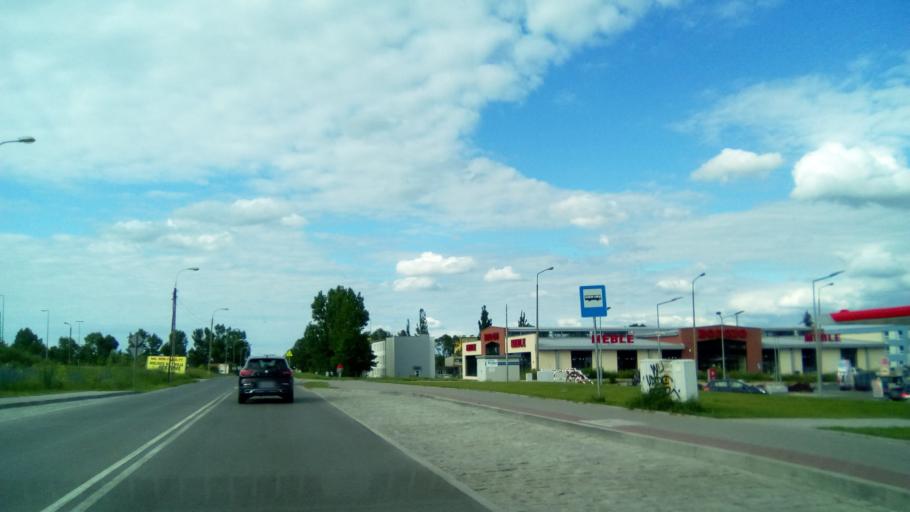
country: PL
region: Greater Poland Voivodeship
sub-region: Powiat gnieznienski
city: Gniezno
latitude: 52.5545
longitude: 17.6059
